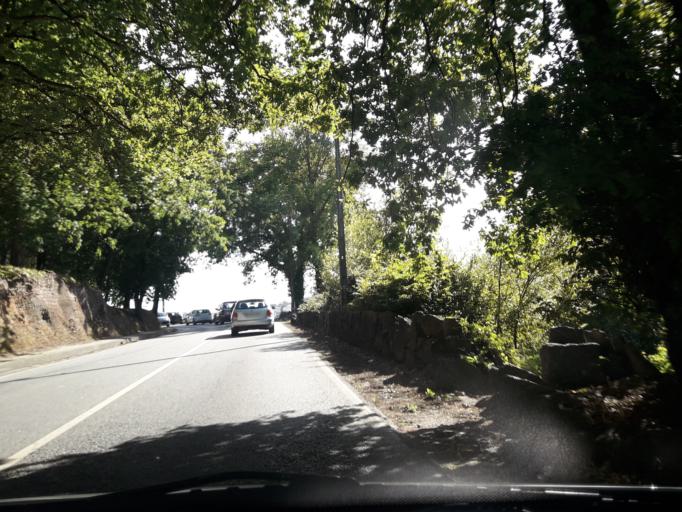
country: PT
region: Braga
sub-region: Vila Nova de Famalicao
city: Vila Nova de Famalicao
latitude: 41.3998
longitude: -8.5153
